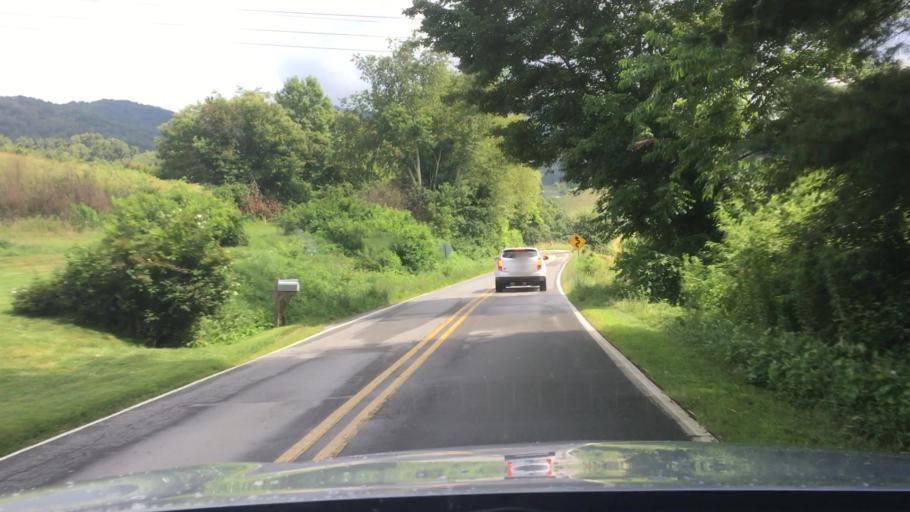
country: US
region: North Carolina
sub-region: Yancey County
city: Burnsville
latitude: 35.9044
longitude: -82.3586
